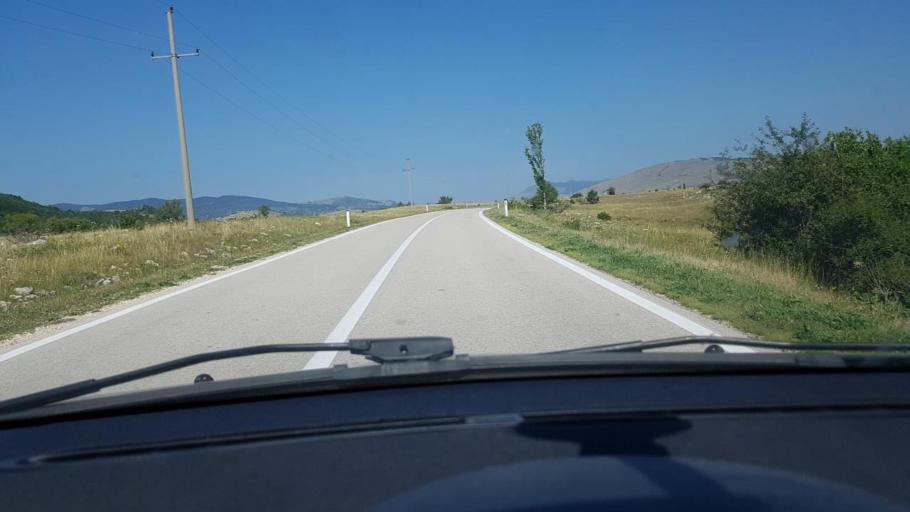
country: BA
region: Federation of Bosnia and Herzegovina
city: Bosansko Grahovo
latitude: 44.1392
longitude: 16.4715
